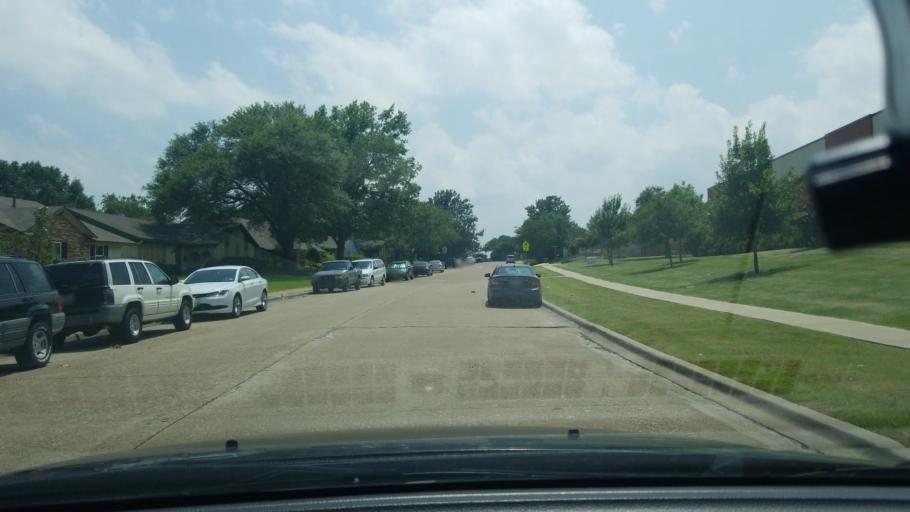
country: US
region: Texas
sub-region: Dallas County
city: Mesquite
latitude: 32.8087
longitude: -96.6428
